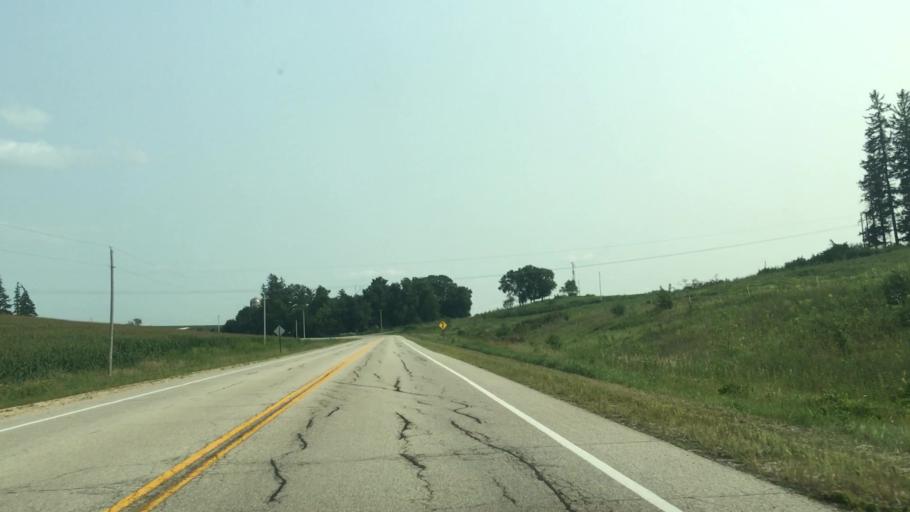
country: US
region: Minnesota
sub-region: Fillmore County
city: Preston
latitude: 43.6946
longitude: -91.9527
